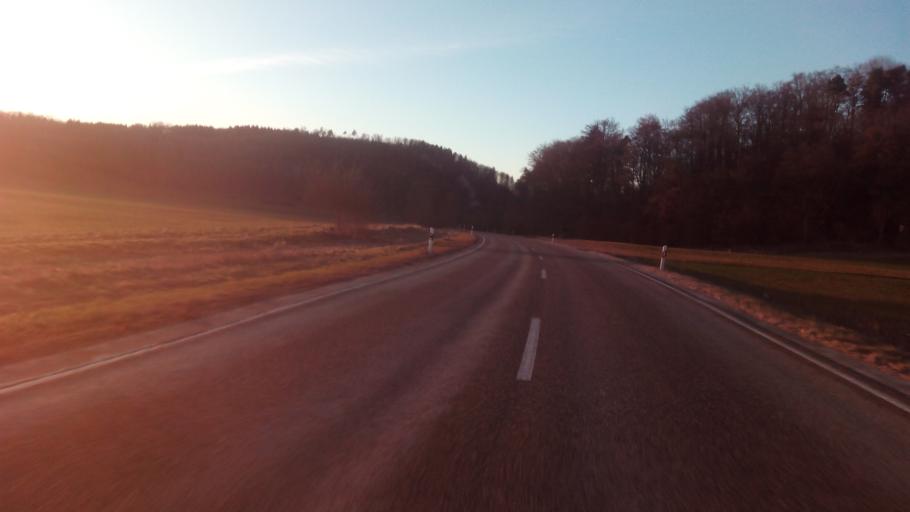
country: DE
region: Baden-Wuerttemberg
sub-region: Tuebingen Region
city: Schelklingen
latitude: 48.3544
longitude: 9.7501
